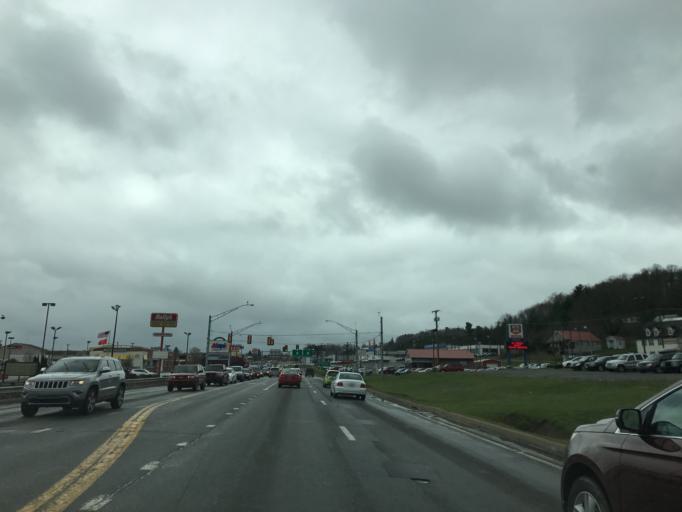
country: US
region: West Virginia
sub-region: Raleigh County
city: Prosperity
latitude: 37.8099
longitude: -81.1855
